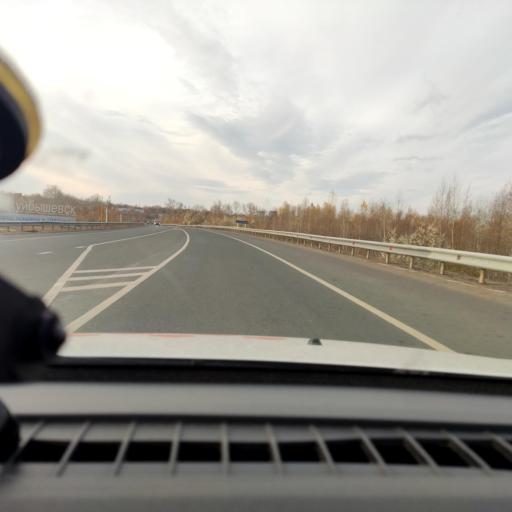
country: RU
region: Samara
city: Novokuybyshevsk
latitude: 53.1267
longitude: 49.9480
